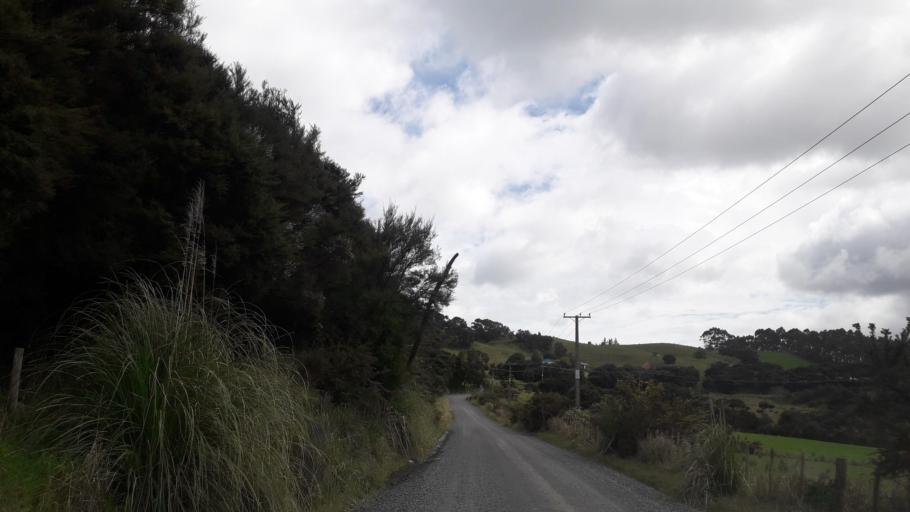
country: NZ
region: Northland
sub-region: Far North District
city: Kaitaia
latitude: -35.1609
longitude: 173.3434
